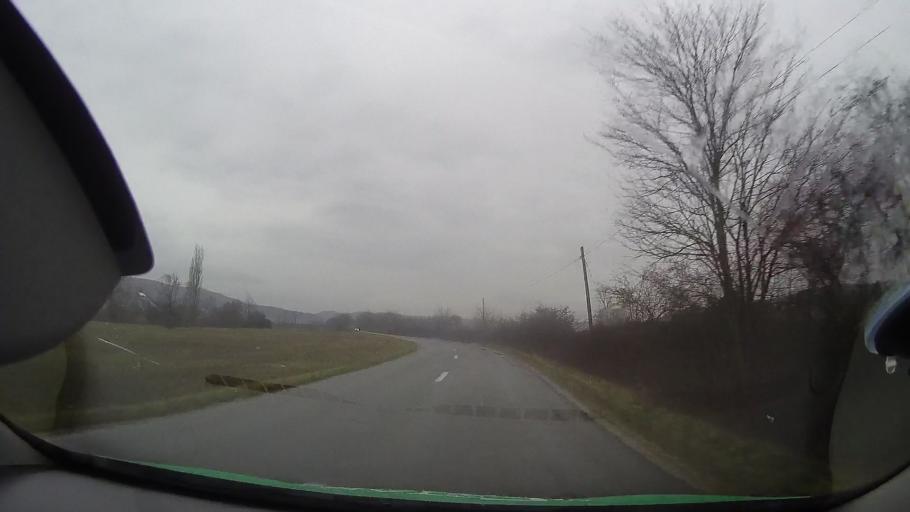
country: RO
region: Bihor
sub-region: Comuna Uileacu de Beius
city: Uileacu de Beius
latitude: 46.6814
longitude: 22.2481
